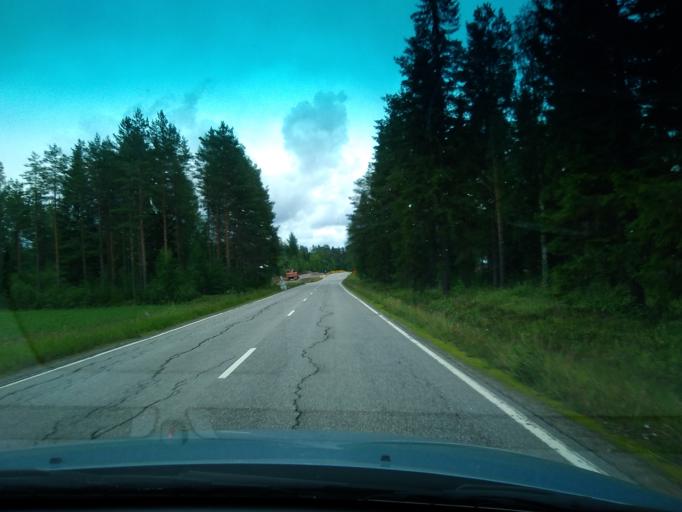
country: FI
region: Central Finland
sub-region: Keuruu
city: Multia
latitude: 62.4156
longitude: 24.7866
